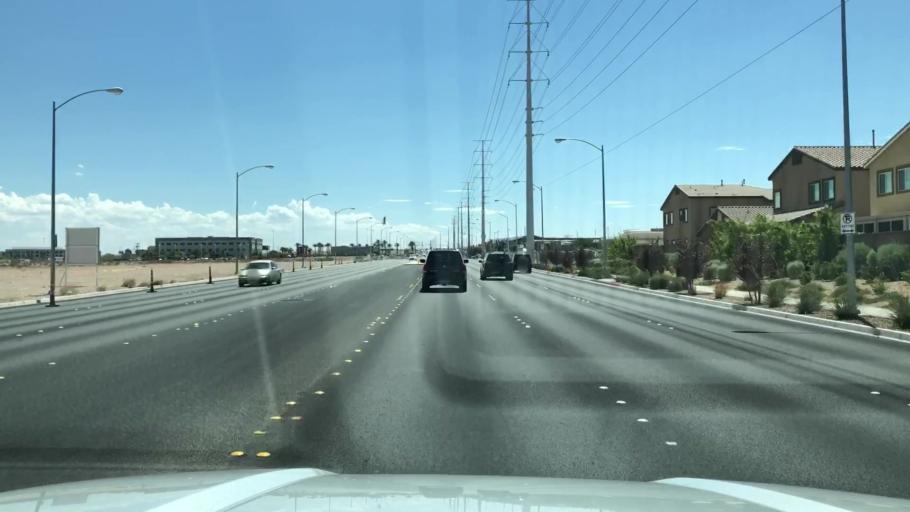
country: US
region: Nevada
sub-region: Clark County
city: Spring Valley
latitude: 36.0768
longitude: -115.2795
